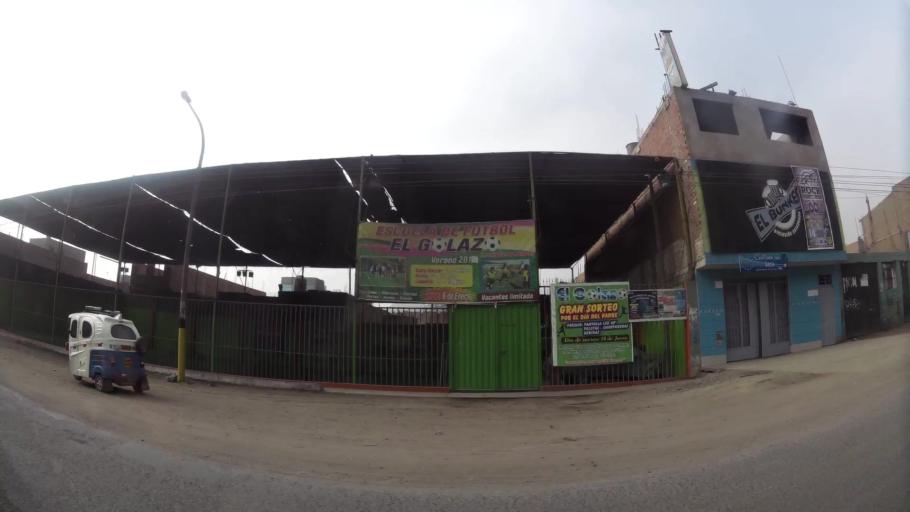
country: PE
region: Lima
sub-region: Lima
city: Santa Maria
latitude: -12.0093
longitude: -76.8307
